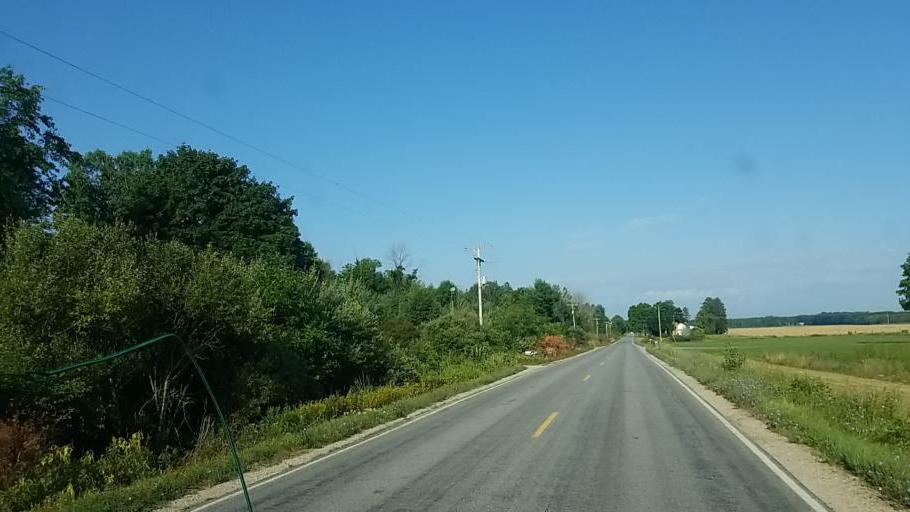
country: US
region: Michigan
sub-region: Newaygo County
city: Newaygo
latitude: 43.3508
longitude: -85.8860
